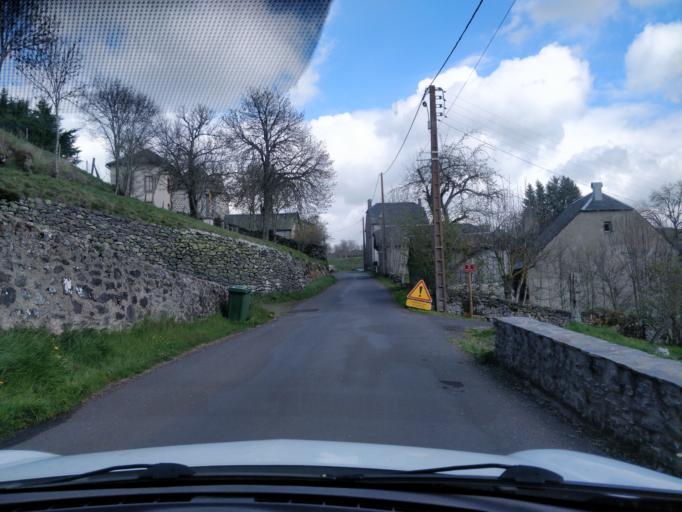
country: FR
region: Auvergne
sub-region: Departement du Cantal
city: Allanche
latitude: 45.2128
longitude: 2.9399
